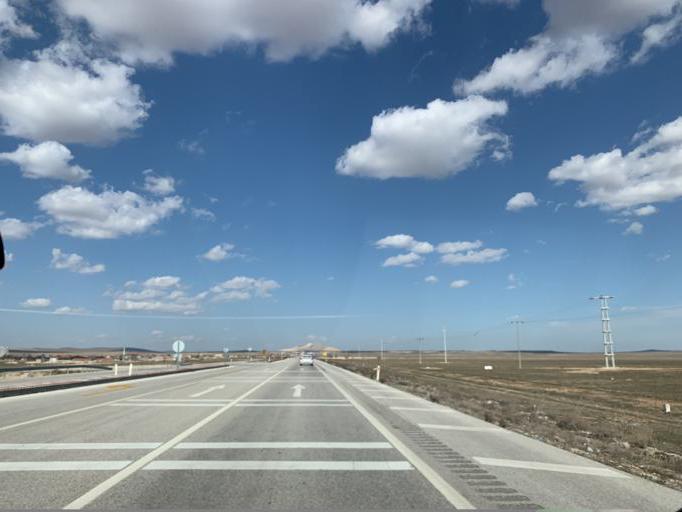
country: TR
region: Konya
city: Cihanbeyli
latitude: 38.5024
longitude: 32.8467
